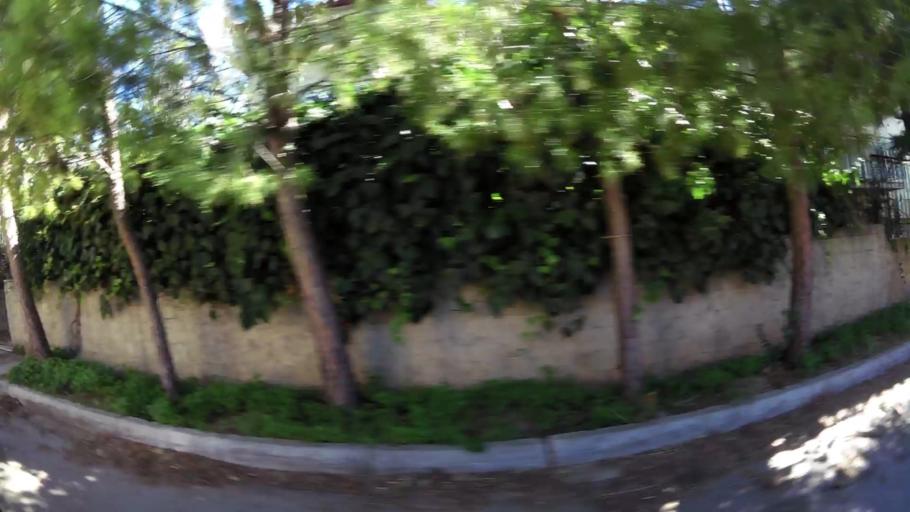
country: GR
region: Attica
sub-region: Nomarchia Athinas
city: Kifisia
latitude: 38.0854
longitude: 23.7963
